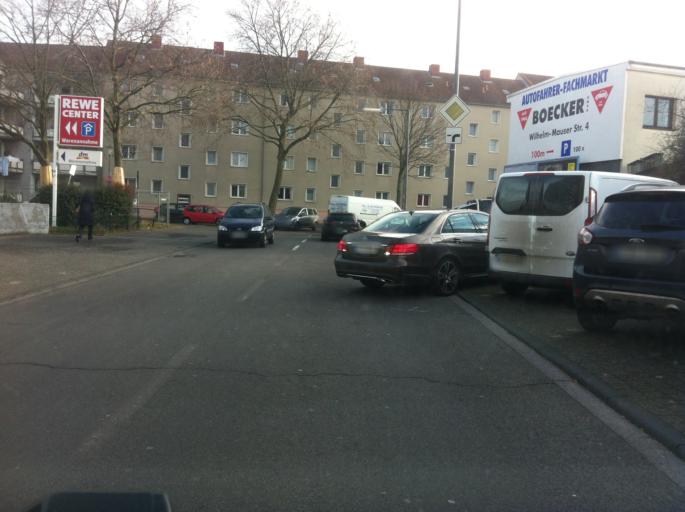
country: DE
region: North Rhine-Westphalia
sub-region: Regierungsbezirk Koln
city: Bilderstoeckchen
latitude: 50.9564
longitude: 6.8995
